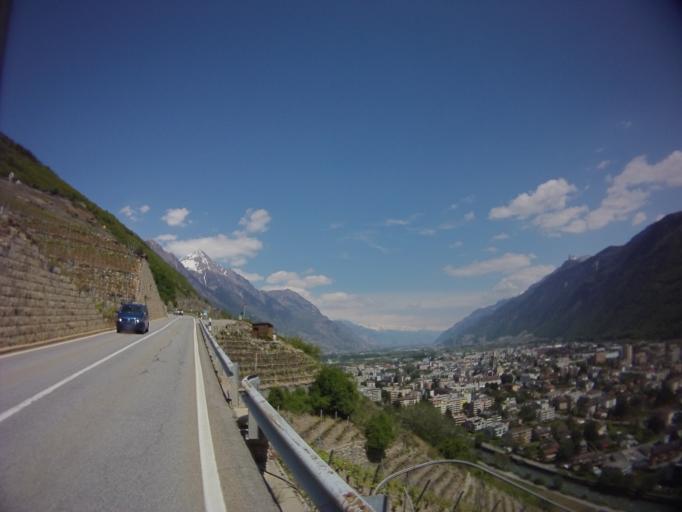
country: CH
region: Valais
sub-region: Martigny District
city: Martigny-Ville
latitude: 46.0960
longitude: 7.0587
